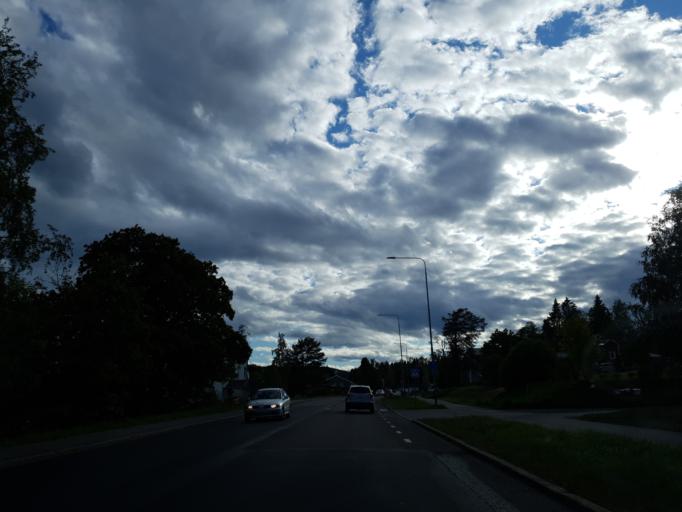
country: SE
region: Vaesternorrland
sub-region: Haernoesands Kommun
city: Haernoesand
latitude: 62.6210
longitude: 17.9154
